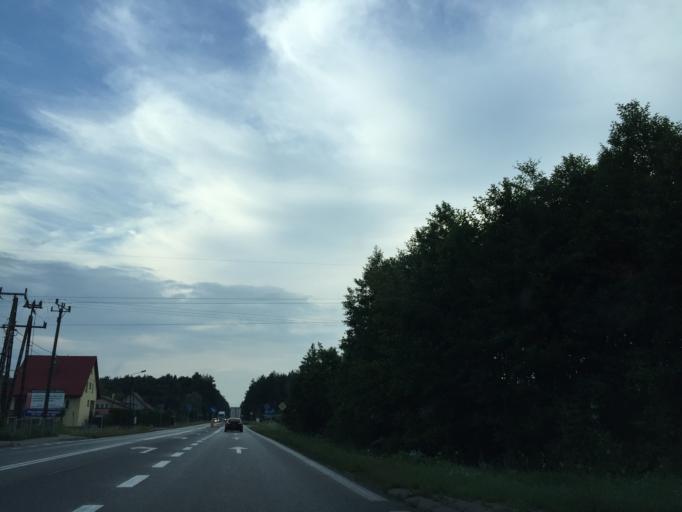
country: PL
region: Masovian Voivodeship
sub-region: Powiat ostrowski
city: Brok
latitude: 52.7039
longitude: 21.8470
